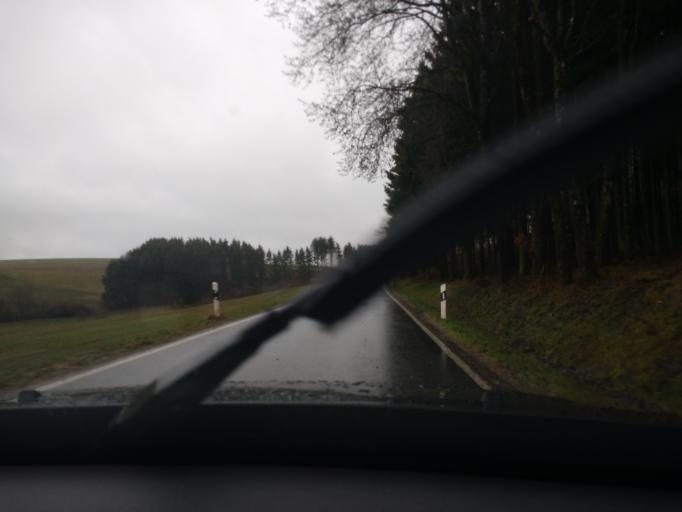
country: DE
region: Rheinland-Pfalz
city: Paschel
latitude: 49.6322
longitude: 6.6836
